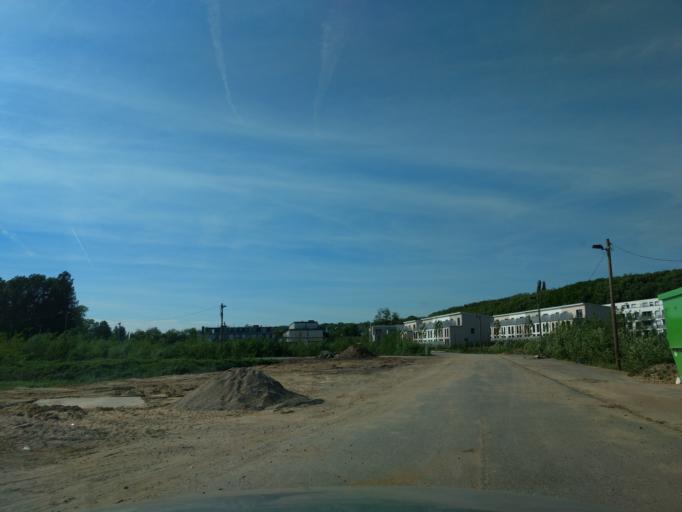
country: DE
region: North Rhine-Westphalia
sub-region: Regierungsbezirk Dusseldorf
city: Erkrath
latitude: 51.2266
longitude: 6.8561
